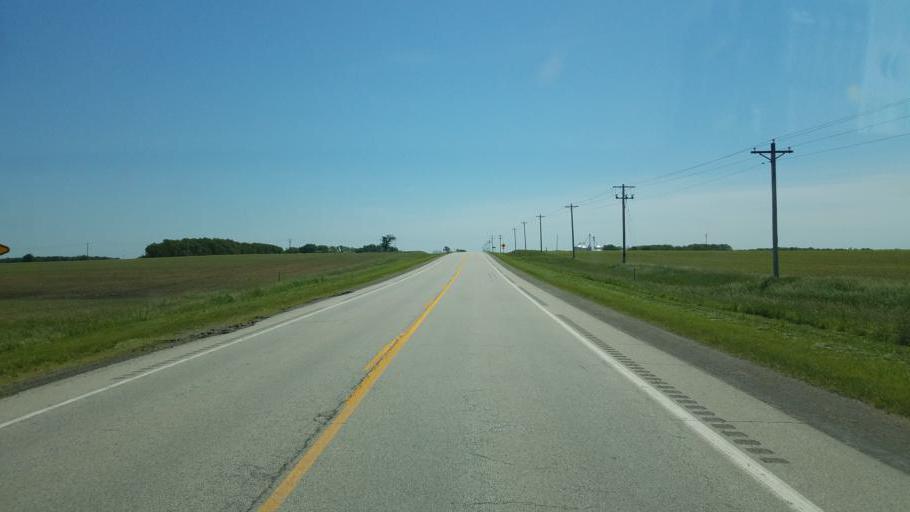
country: US
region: Illinois
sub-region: McLean County
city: Le Roy
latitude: 40.3118
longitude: -88.7975
